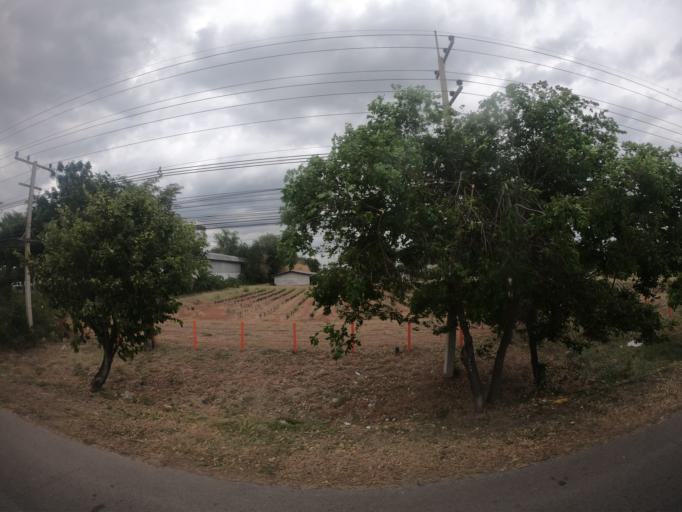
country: TH
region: Nakhon Ratchasima
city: Nakhon Ratchasima
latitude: 14.8760
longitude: 102.1770
